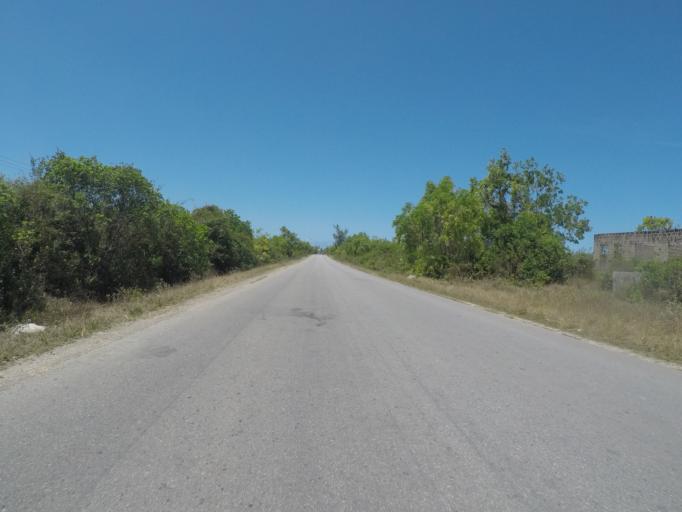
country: TZ
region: Zanzibar Central/South
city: Nganane
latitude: -6.2678
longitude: 39.5226
